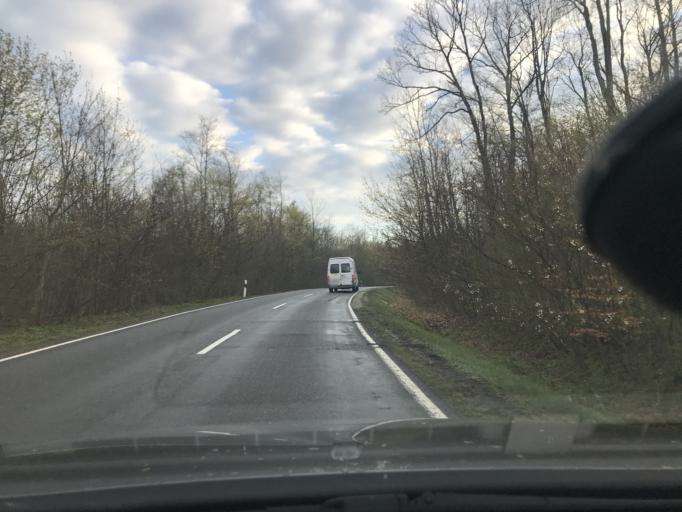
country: DE
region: Thuringia
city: Menteroda
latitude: 51.2970
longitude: 10.5531
